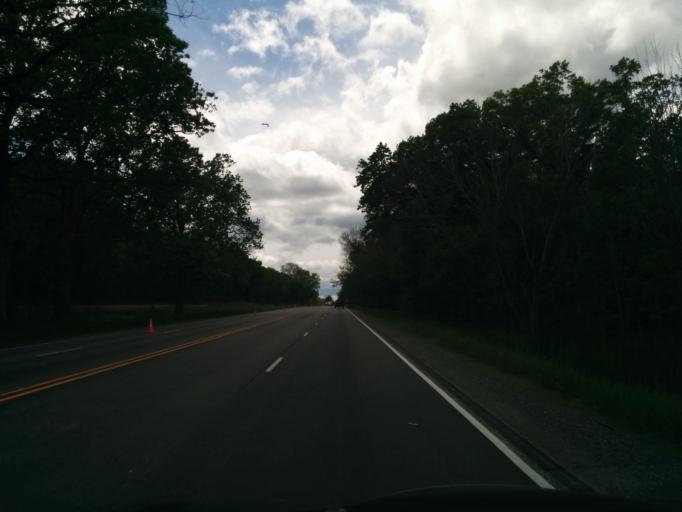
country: US
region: Indiana
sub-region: Porter County
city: Chesterton
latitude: 41.6624
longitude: -86.9895
